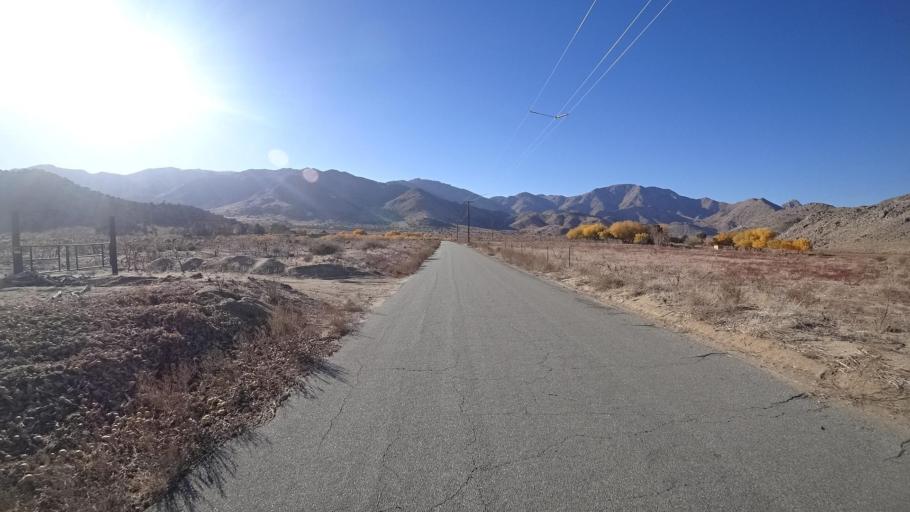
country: US
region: California
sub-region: Kern County
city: Weldon
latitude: 35.5576
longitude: -118.2329
